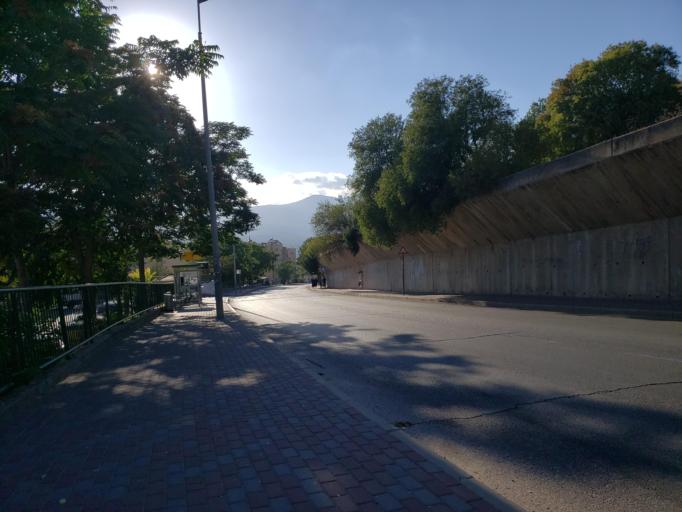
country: IL
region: Northern District
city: Safed
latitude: 32.9650
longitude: 35.4908
